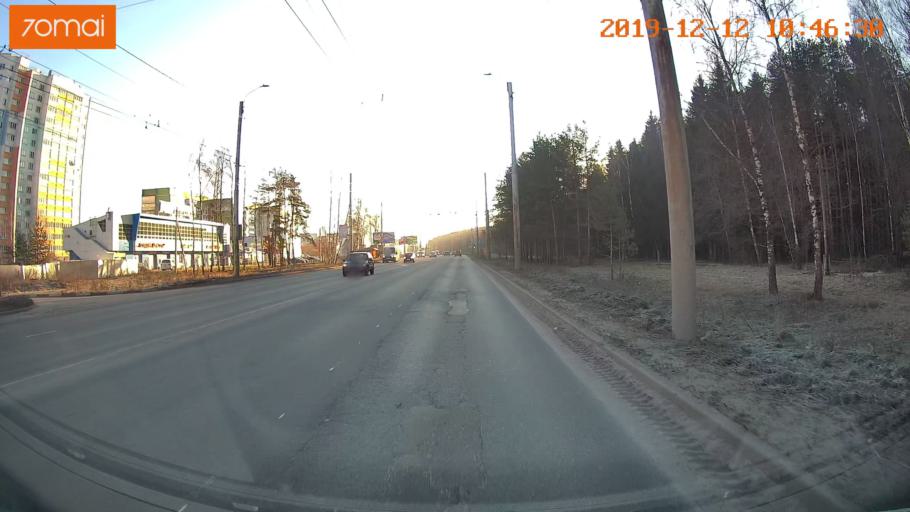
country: RU
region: Ivanovo
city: Kokhma
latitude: 56.9532
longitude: 41.0447
